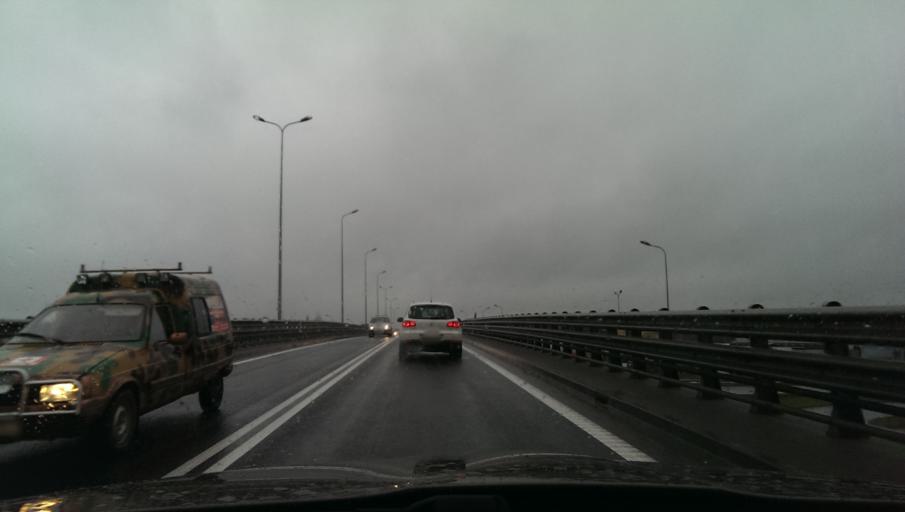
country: PL
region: Subcarpathian Voivodeship
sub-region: Powiat rzeszowski
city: Rudna Mala
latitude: 50.1139
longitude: 21.9733
